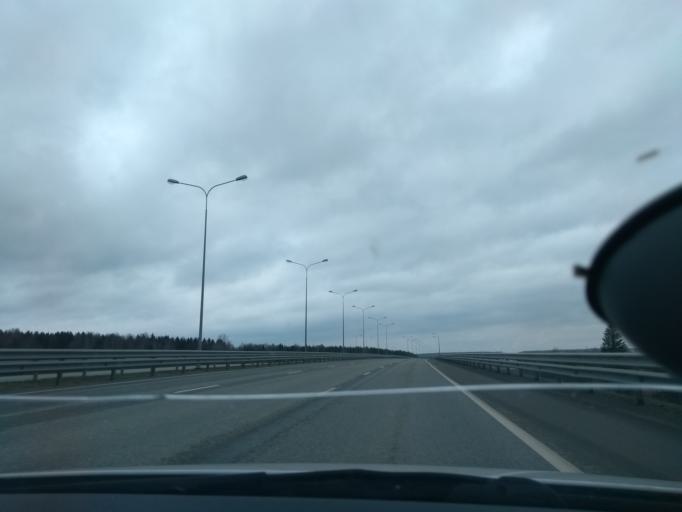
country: RU
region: Perm
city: Bershet'
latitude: 57.7052
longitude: 56.3707
